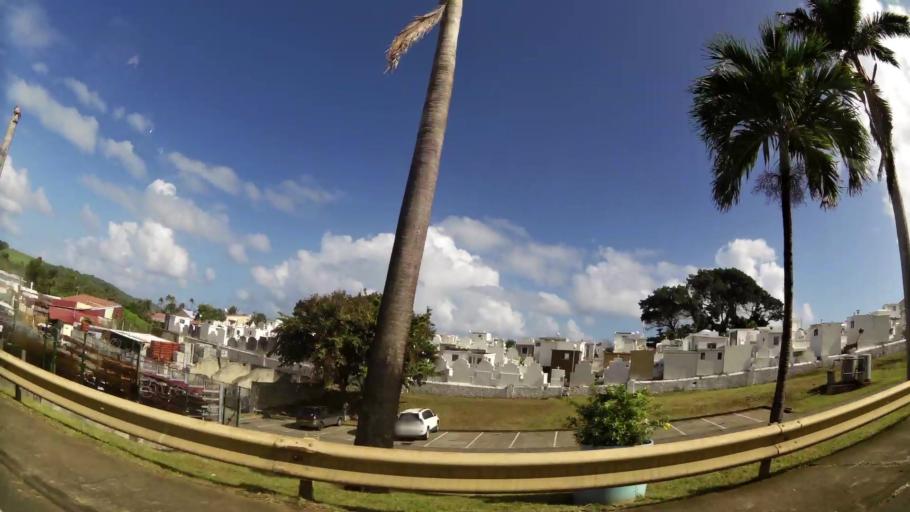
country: MQ
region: Martinique
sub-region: Martinique
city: Sainte-Marie
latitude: 14.7835
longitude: -60.9946
